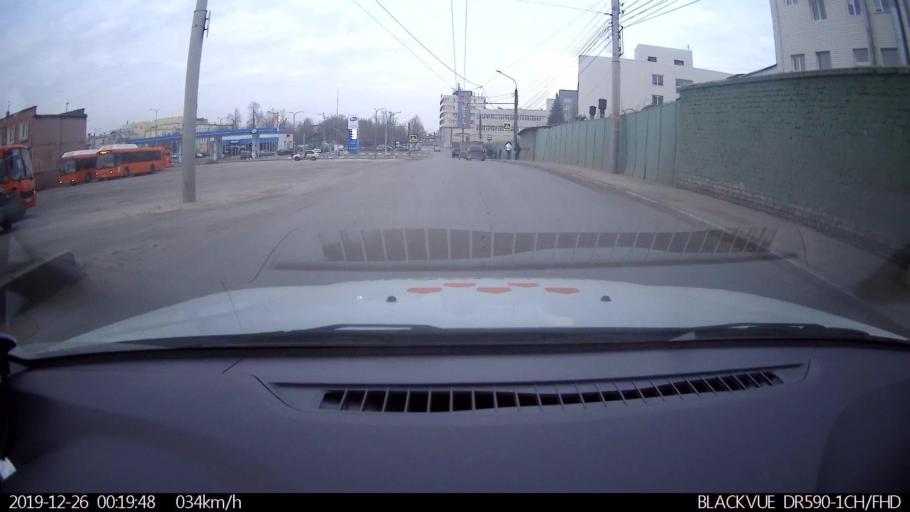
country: RU
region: Nizjnij Novgorod
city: Nizhniy Novgorod
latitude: 56.3129
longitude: 43.9459
